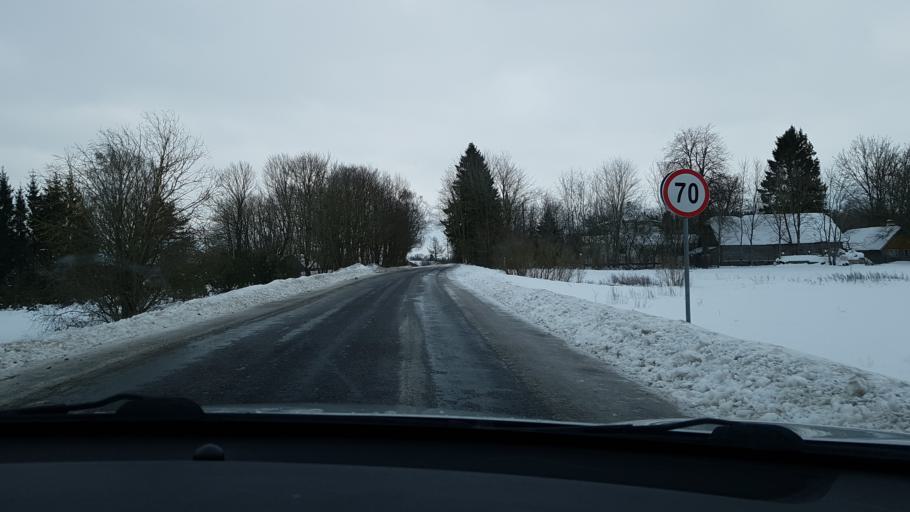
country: EE
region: Jaervamaa
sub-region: Koeru vald
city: Koeru
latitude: 58.9745
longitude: 26.0047
